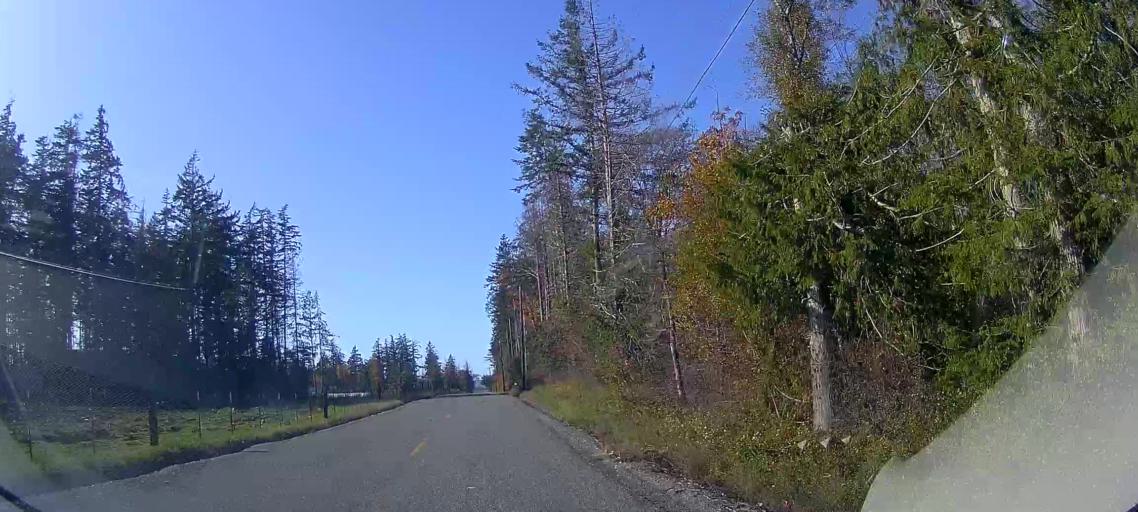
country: US
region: Washington
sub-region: Skagit County
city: Mount Vernon
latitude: 48.3700
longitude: -122.4397
